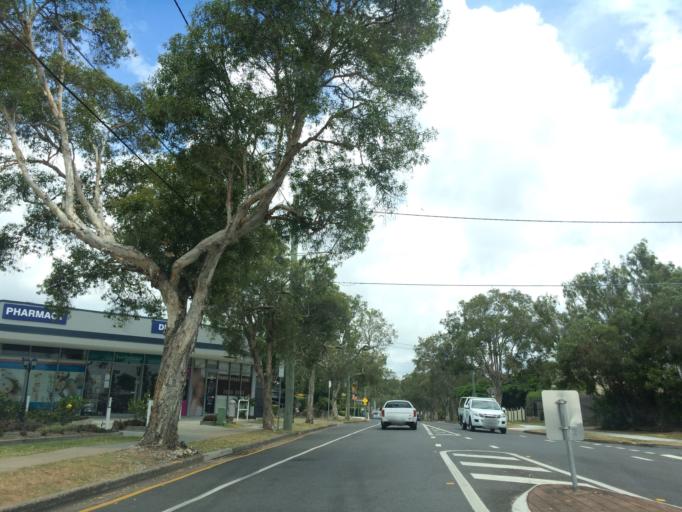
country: AU
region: Queensland
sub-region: Brisbane
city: Balmoral
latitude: -27.4618
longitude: 153.0635
